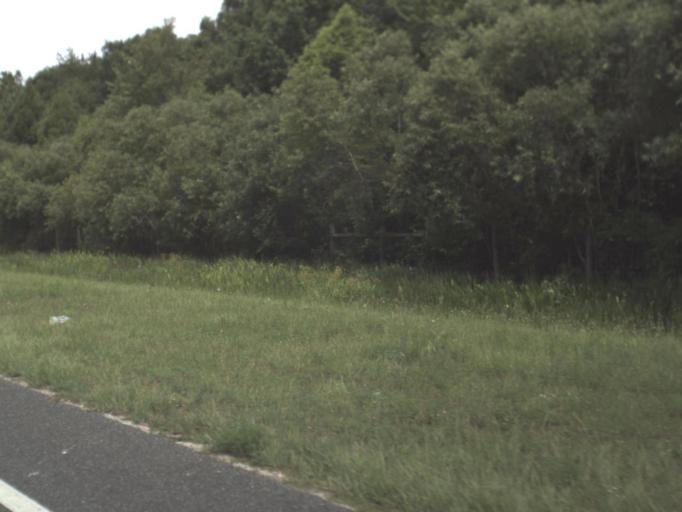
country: US
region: Florida
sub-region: Putnam County
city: Palatka
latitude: 29.6299
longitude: -81.7534
